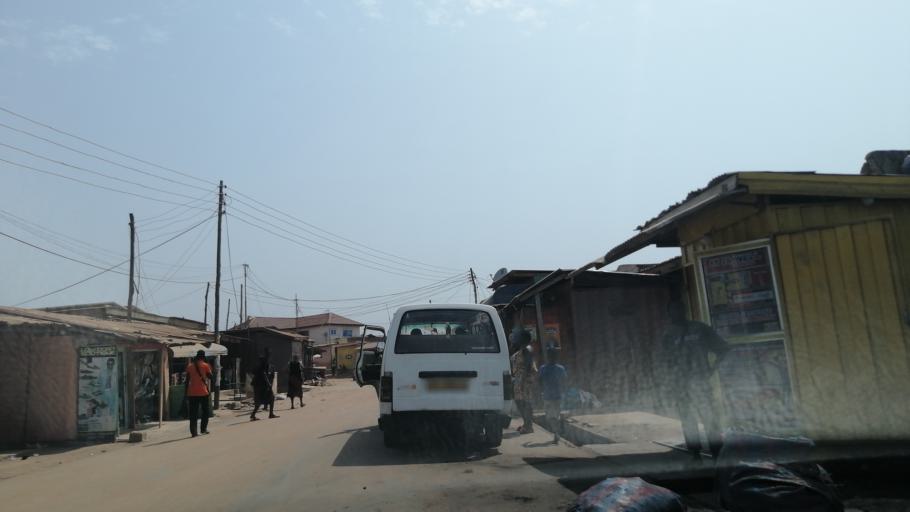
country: GH
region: Greater Accra
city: Dome
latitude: 5.6577
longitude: -0.2676
